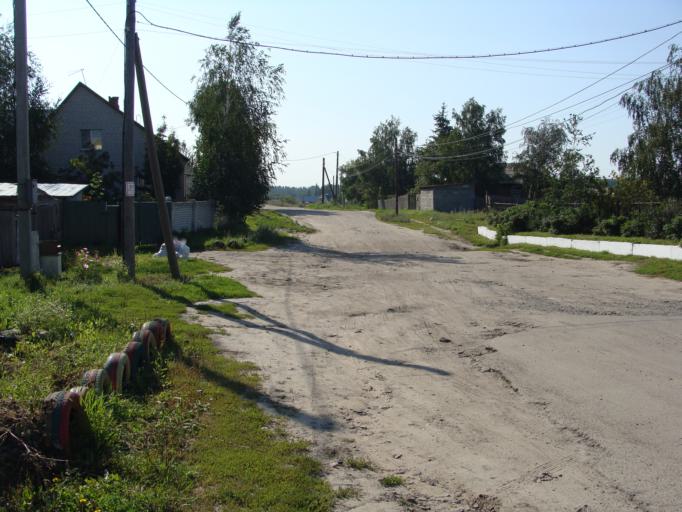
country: RU
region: Altai Krai
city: Vlasikha
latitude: 53.2962
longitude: 83.5829
